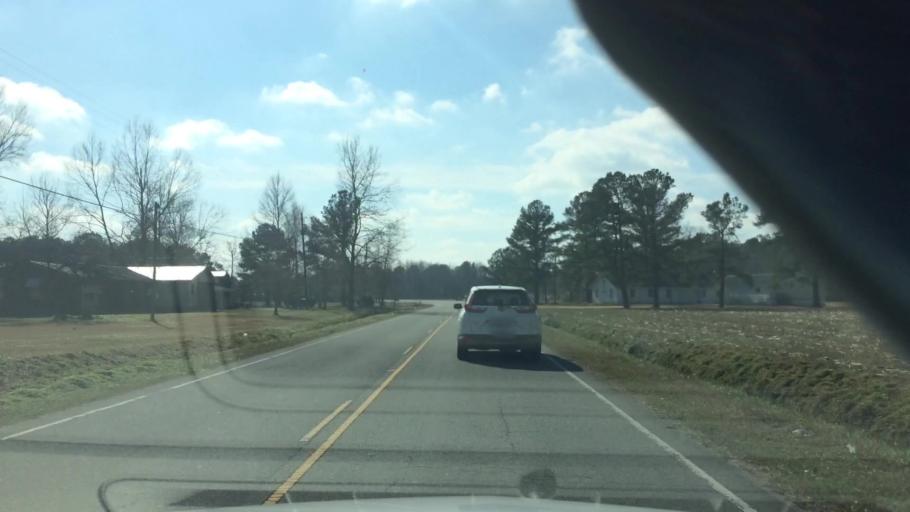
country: US
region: North Carolina
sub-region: Duplin County
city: Beulaville
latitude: 34.8833
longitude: -77.7877
